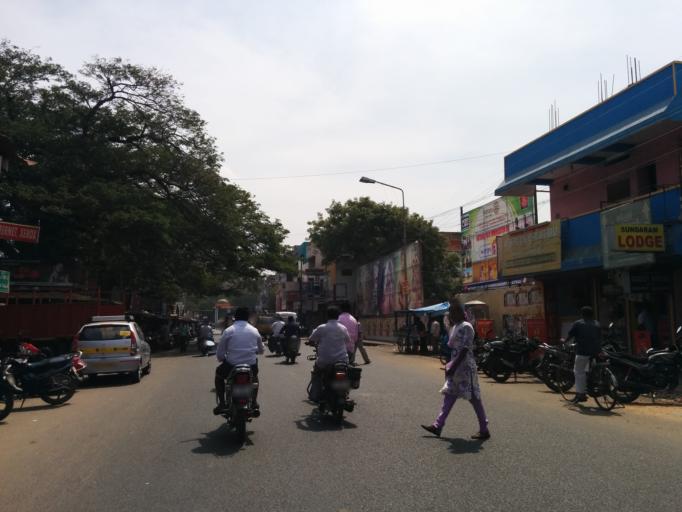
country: IN
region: Pondicherry
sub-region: Puducherry
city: Puducherry
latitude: 11.9322
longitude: 79.8242
